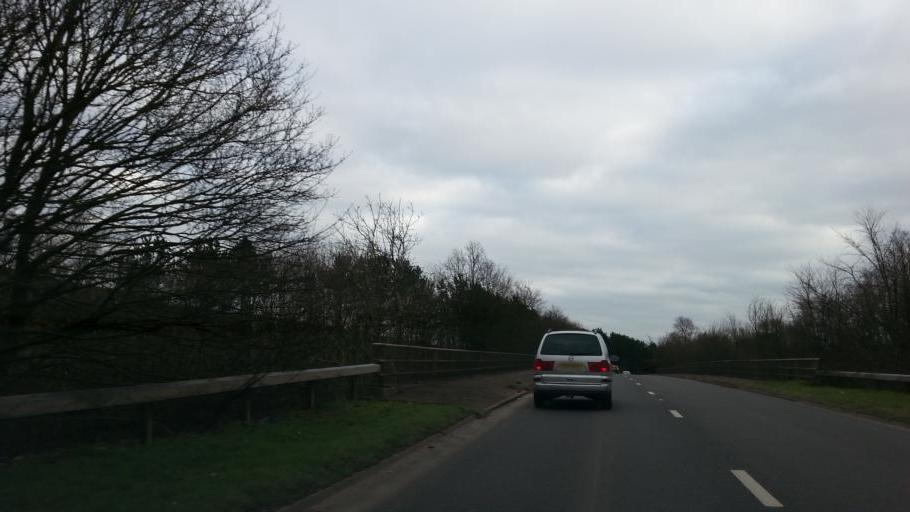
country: GB
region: England
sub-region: Solihull
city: Bickenhill
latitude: 52.4600
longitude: -1.7032
